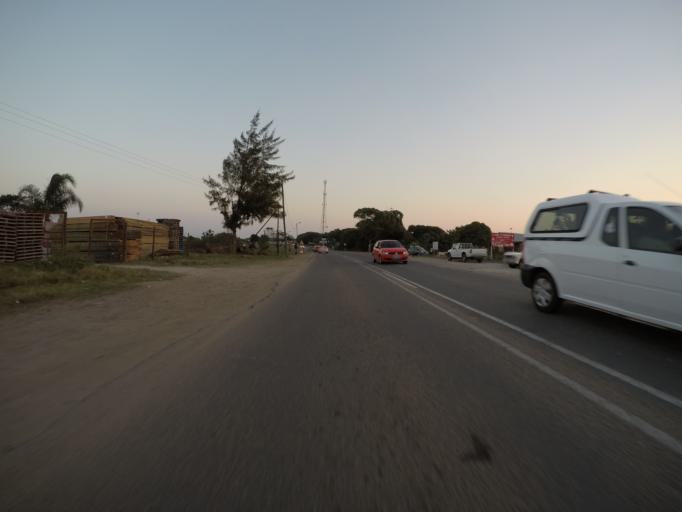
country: ZA
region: KwaZulu-Natal
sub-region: uThungulu District Municipality
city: Richards Bay
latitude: -28.7587
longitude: 32.1332
